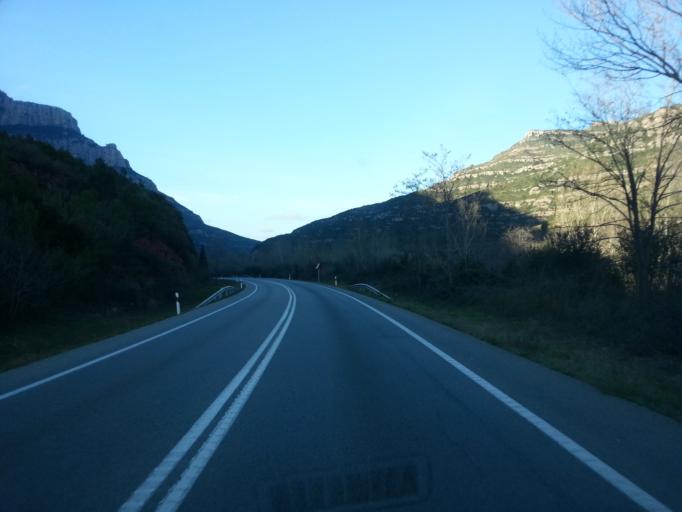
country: ES
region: Catalonia
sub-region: Provincia de Barcelona
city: Collbato
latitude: 41.5799
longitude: 1.8592
